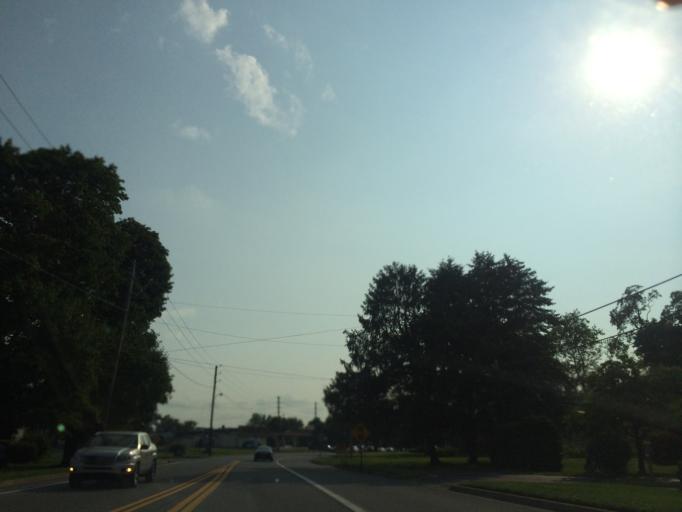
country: US
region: Pennsylvania
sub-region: Perry County
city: Marysville
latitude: 40.3251
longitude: -76.8966
